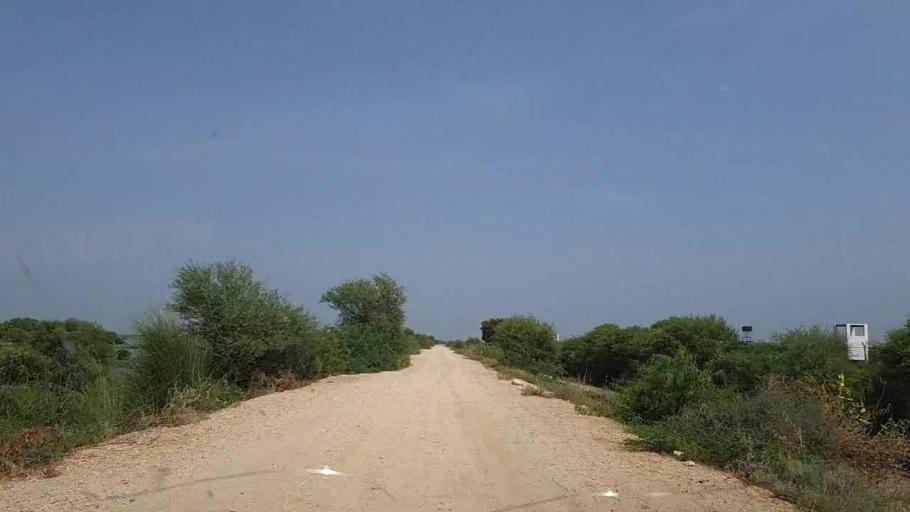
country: PK
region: Sindh
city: Ghotki
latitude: 28.1157
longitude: 69.3853
